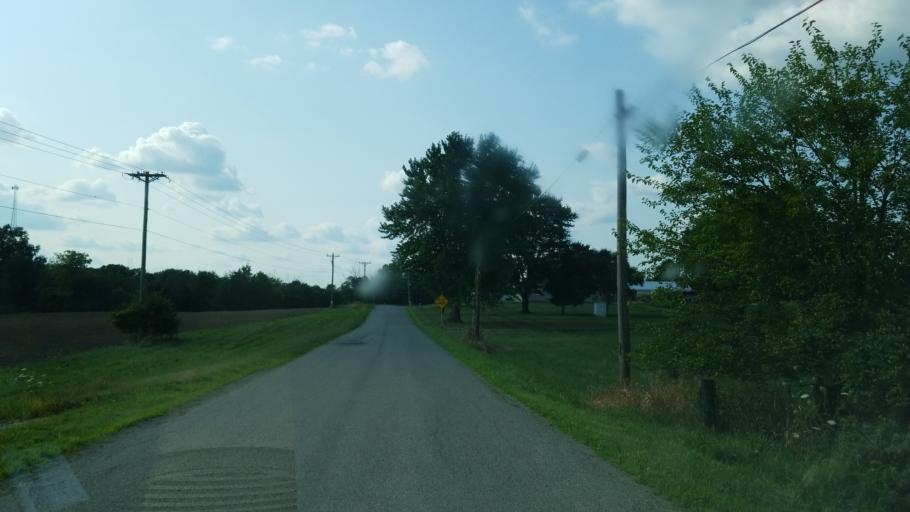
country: US
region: Ohio
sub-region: Union County
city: New California
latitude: 40.1400
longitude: -83.2463
